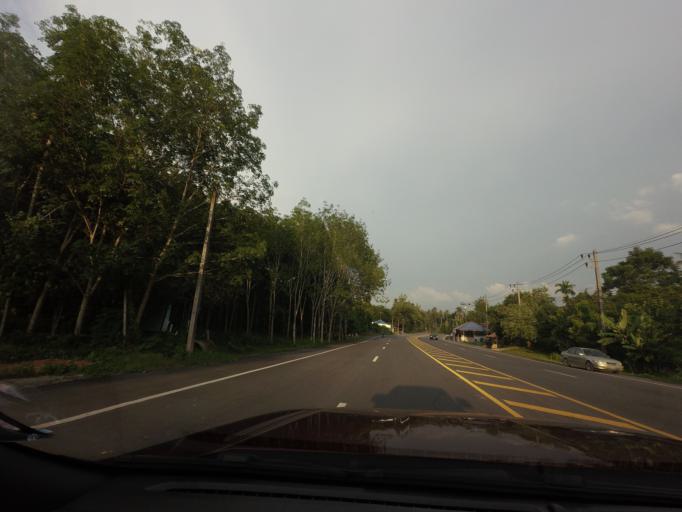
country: TH
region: Pattani
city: Khok Pho
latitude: 6.6770
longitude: 101.1241
